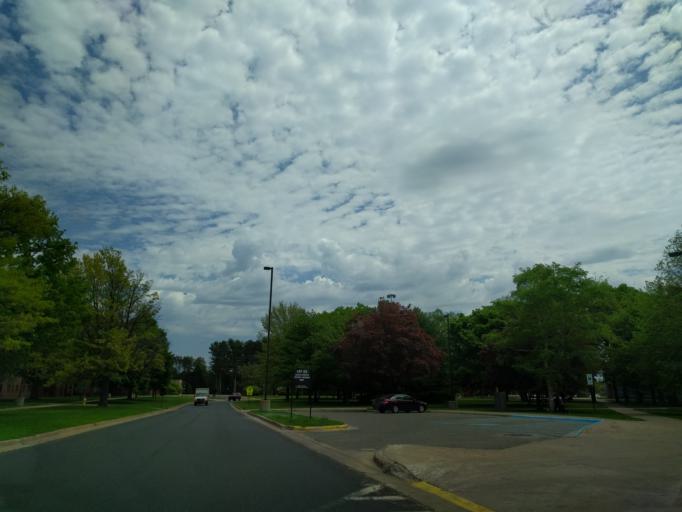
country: US
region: Michigan
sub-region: Marquette County
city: Marquette
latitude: 46.5576
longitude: -87.4020
